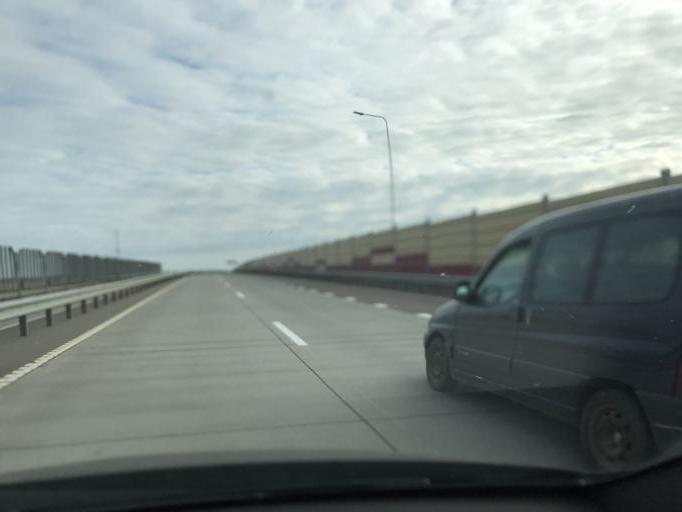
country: BY
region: Minsk
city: Syomkava
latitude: 54.0677
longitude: 27.4495
